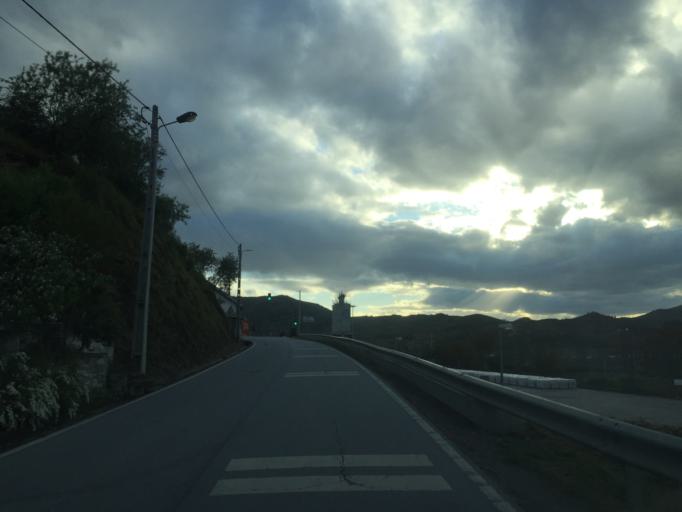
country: PT
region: Braganca
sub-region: Torre de Moncorvo
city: Torre de Moncorvo
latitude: 41.1314
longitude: -7.1202
